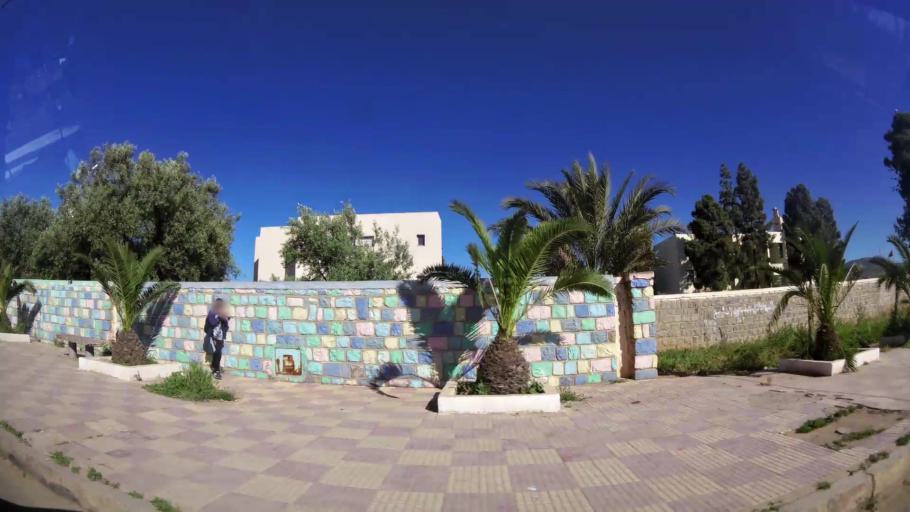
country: MA
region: Oriental
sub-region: Berkane-Taourirt
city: Ahfir
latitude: 34.9490
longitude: -2.1026
